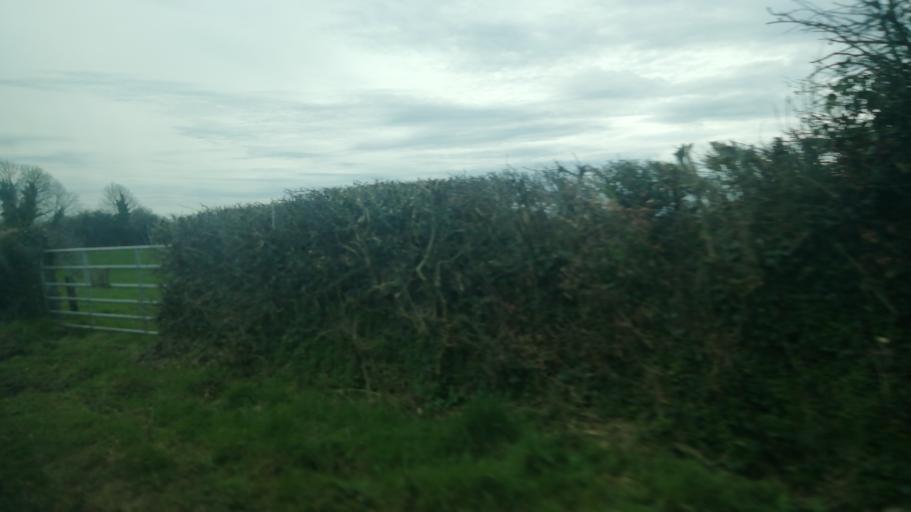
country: IE
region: Leinster
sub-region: Kildare
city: Derrinturn
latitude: 53.3483
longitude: -6.9553
